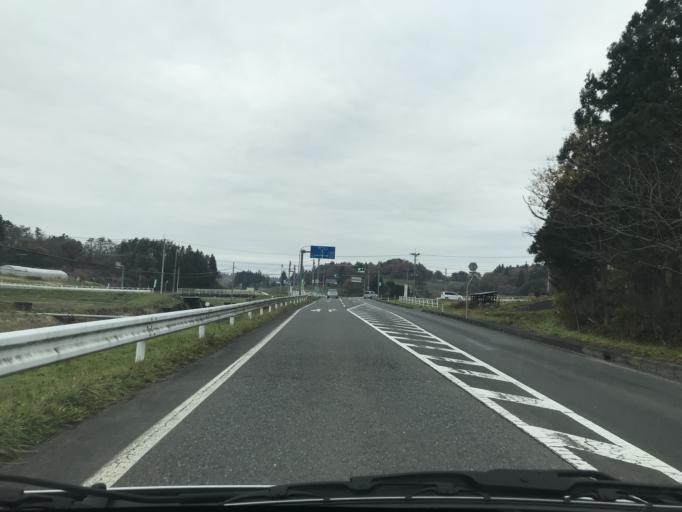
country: JP
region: Iwate
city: Mizusawa
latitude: 39.1899
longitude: 141.2227
